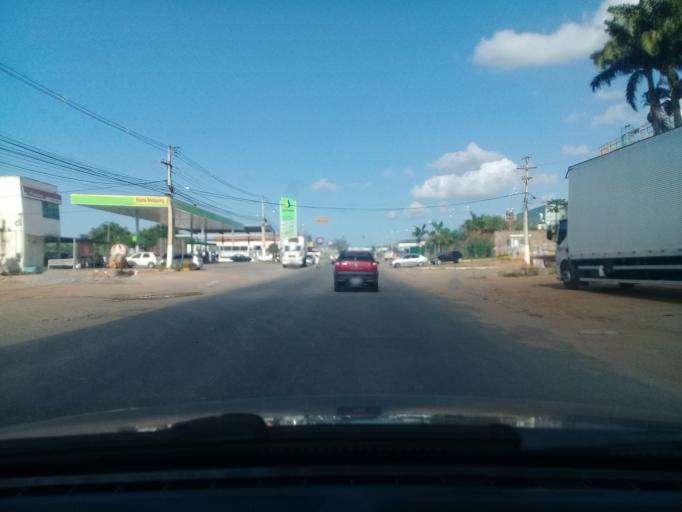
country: BR
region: Pernambuco
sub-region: Vitoria De Santo Antao
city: Vitoria de Santo Antao
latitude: -8.1153
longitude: -35.2729
